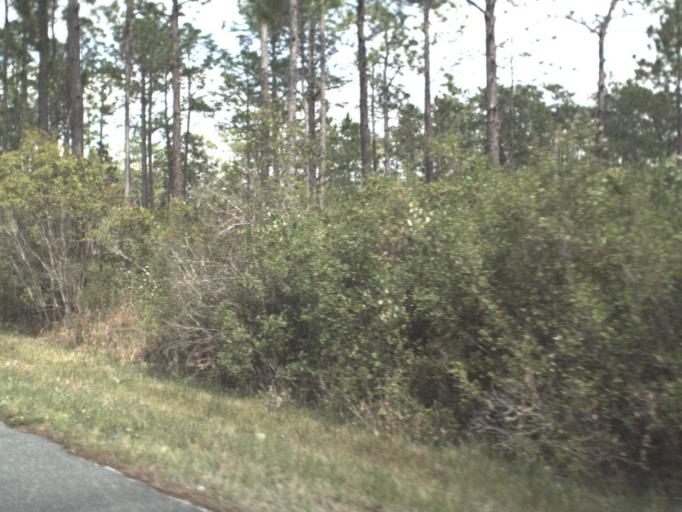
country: US
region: Florida
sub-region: Franklin County
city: Apalachicola
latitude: 29.9827
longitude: -84.9757
